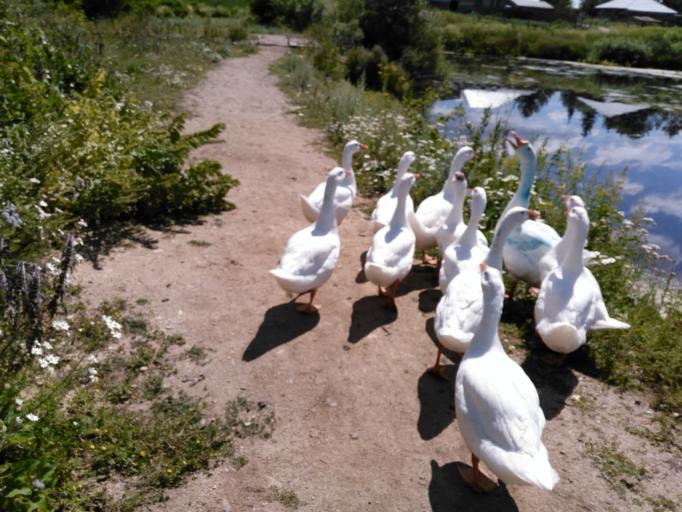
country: RU
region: Bashkortostan
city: Akhunovo
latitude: 54.2093
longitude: 59.5995
